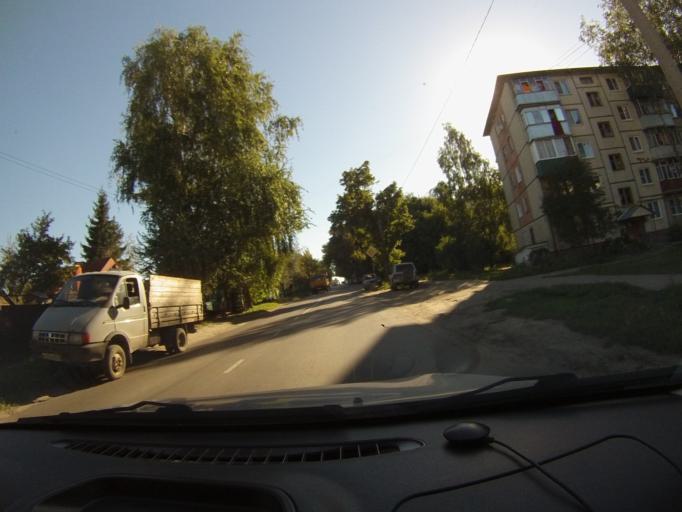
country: RU
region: Tambov
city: Tambov
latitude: 52.7498
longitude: 41.4228
